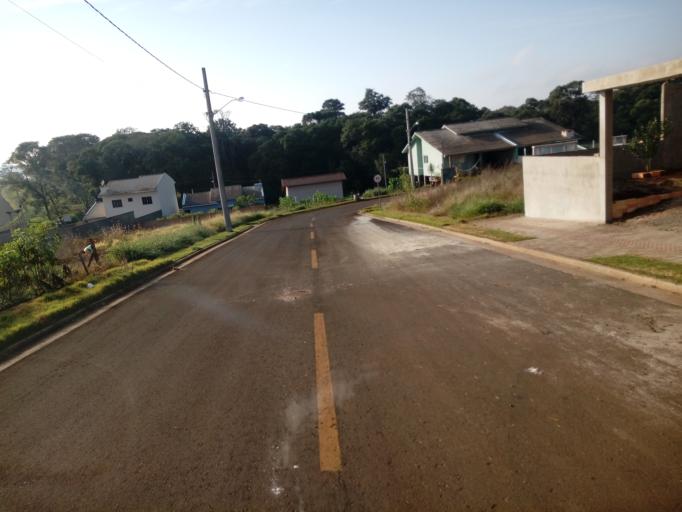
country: BR
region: Santa Catarina
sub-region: Chapeco
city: Chapeco
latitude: -27.0910
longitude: -52.7118
